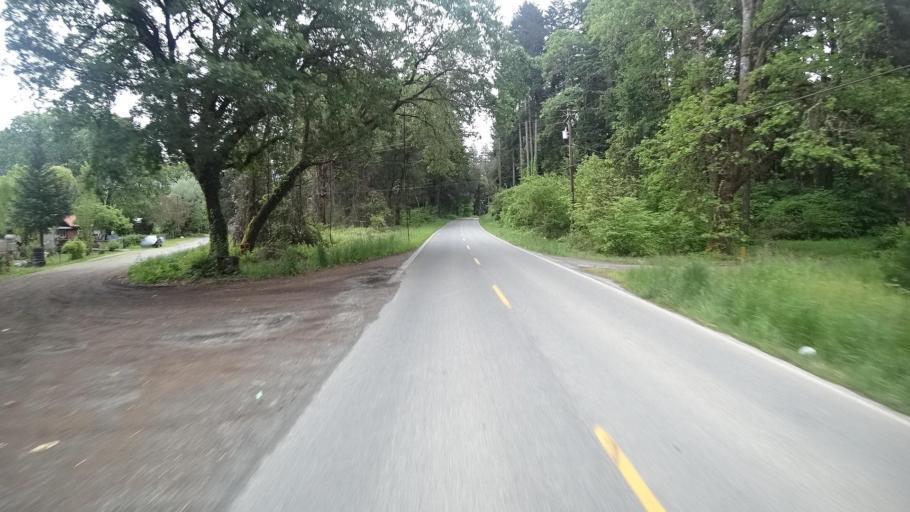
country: US
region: California
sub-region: Humboldt County
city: Willow Creek
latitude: 41.0848
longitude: -123.7054
